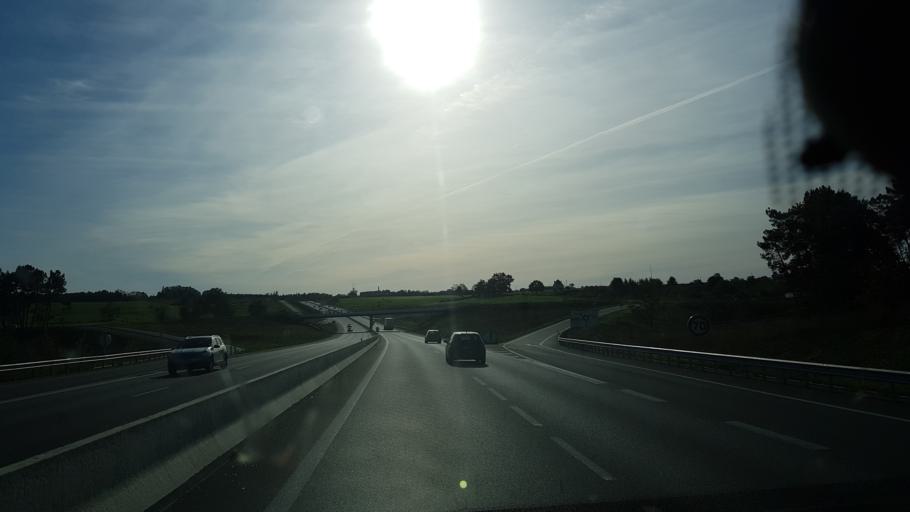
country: FR
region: Poitou-Charentes
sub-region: Departement de la Charente
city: Baignes-Sainte-Radegonde
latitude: 45.3601
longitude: -0.1922
